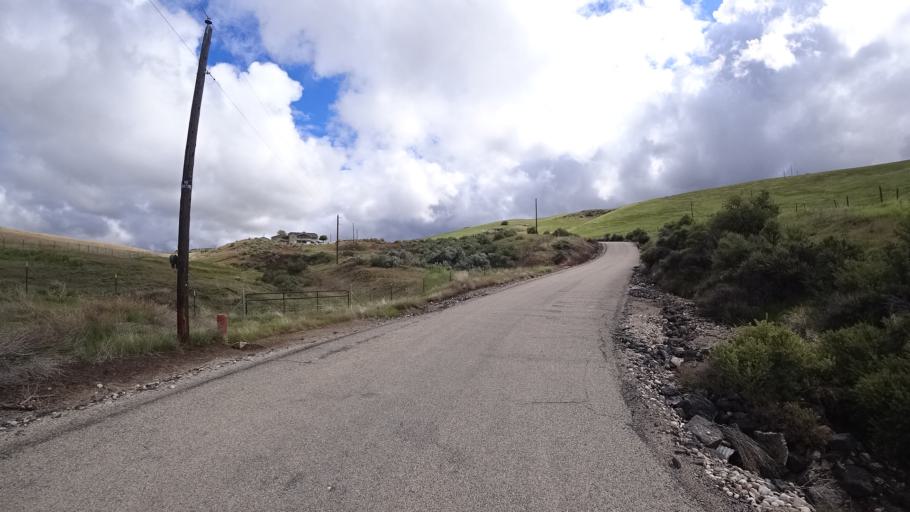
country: US
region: Idaho
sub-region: Ada County
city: Garden City
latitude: 43.7356
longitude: -116.2285
